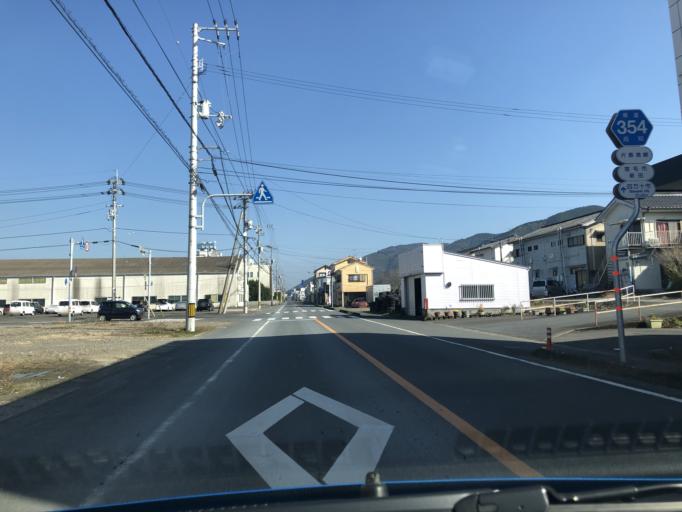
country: JP
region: Kochi
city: Sukumo
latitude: 32.9273
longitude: 132.7086
